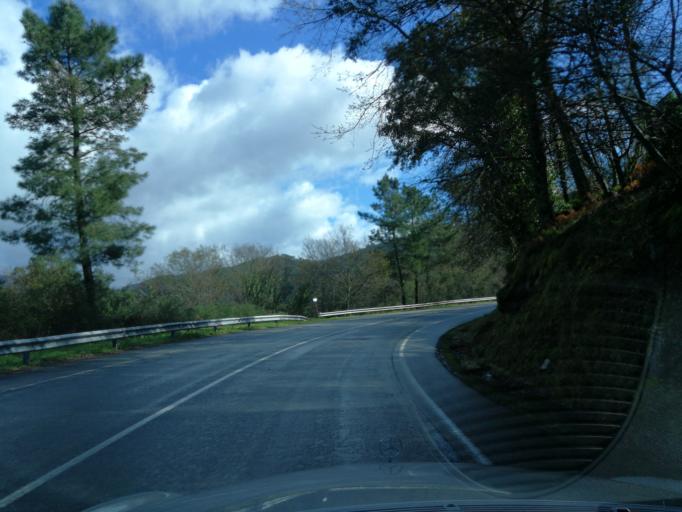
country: PT
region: Braga
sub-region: Terras de Bouro
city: Antas
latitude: 41.8403
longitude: -8.2937
